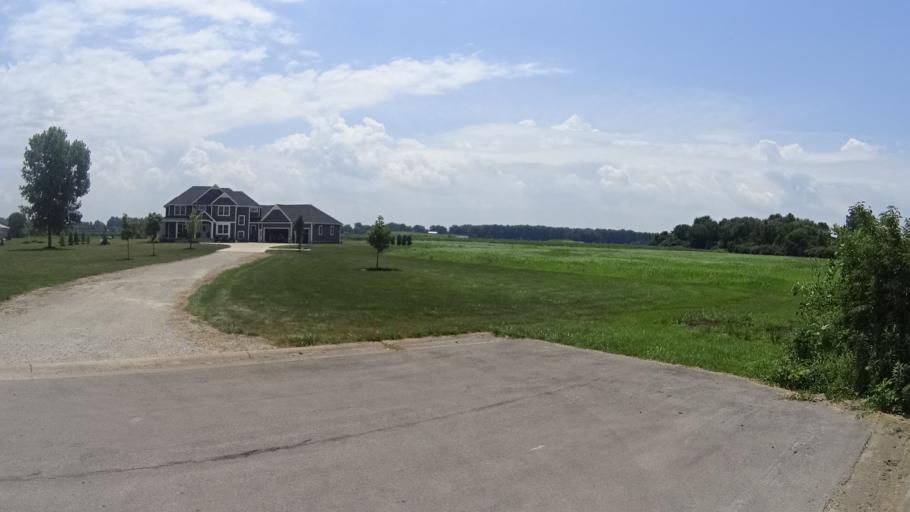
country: US
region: Ohio
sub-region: Erie County
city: Huron
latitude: 41.4109
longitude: -82.6214
